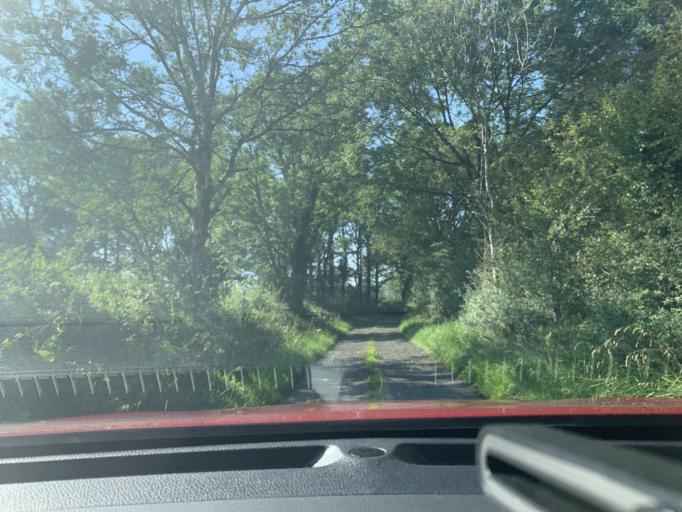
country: IE
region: Connaught
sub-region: Sligo
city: Tobercurry
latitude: 54.0615
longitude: -8.7958
